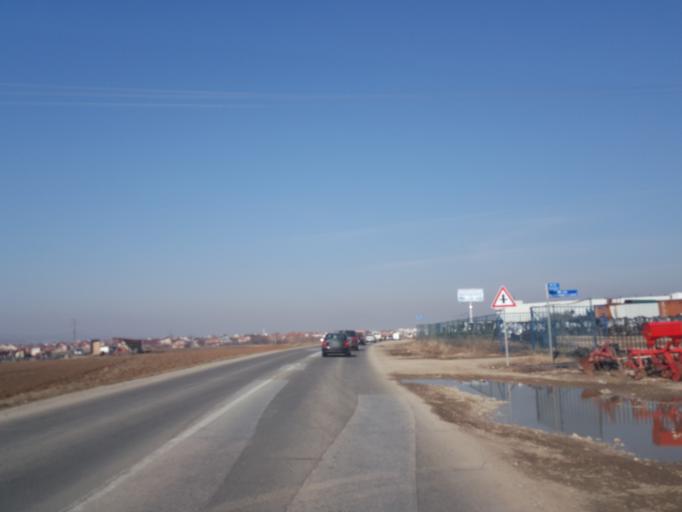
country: XK
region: Mitrovica
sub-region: Vushtrri
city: Vushtrri
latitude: 42.7752
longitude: 21.0162
